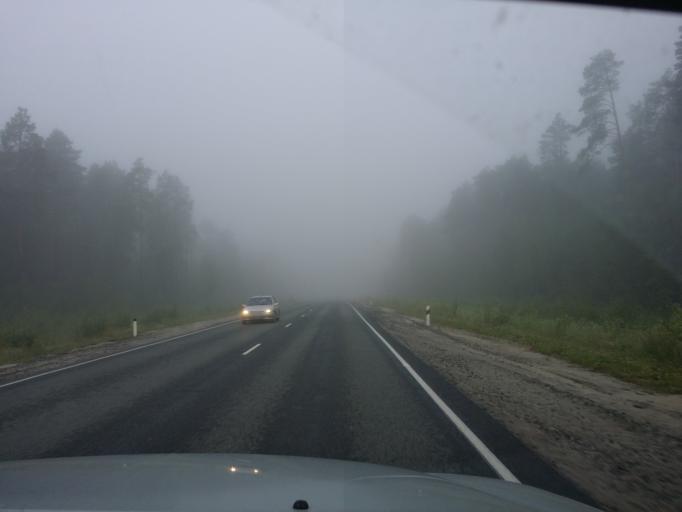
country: RU
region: Khanty-Mansiyskiy Avtonomnyy Okrug
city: Gornopravdinsk
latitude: 59.6587
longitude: 69.9531
